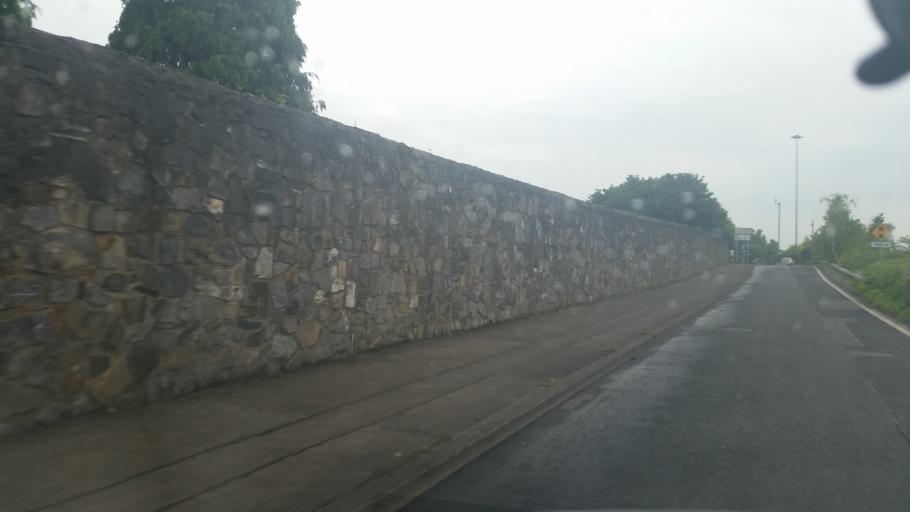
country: IE
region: Leinster
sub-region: Dublin City
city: Finglas
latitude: 53.3888
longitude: -6.3003
